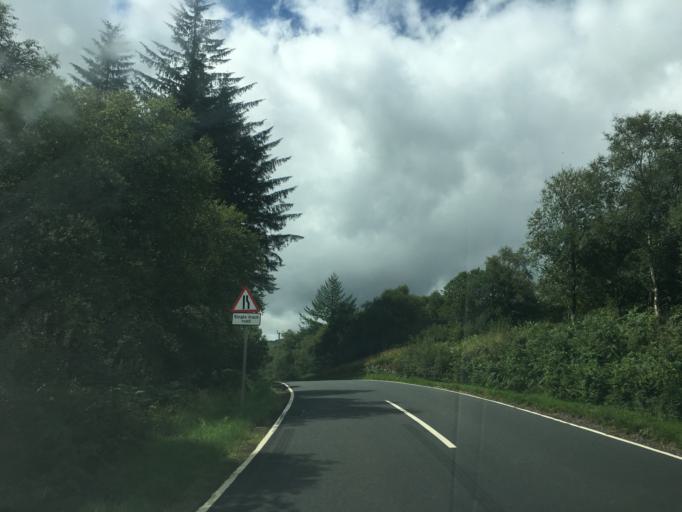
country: GB
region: Scotland
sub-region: Argyll and Bute
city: Port Bannatyne
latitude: 56.0008
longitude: -5.1017
